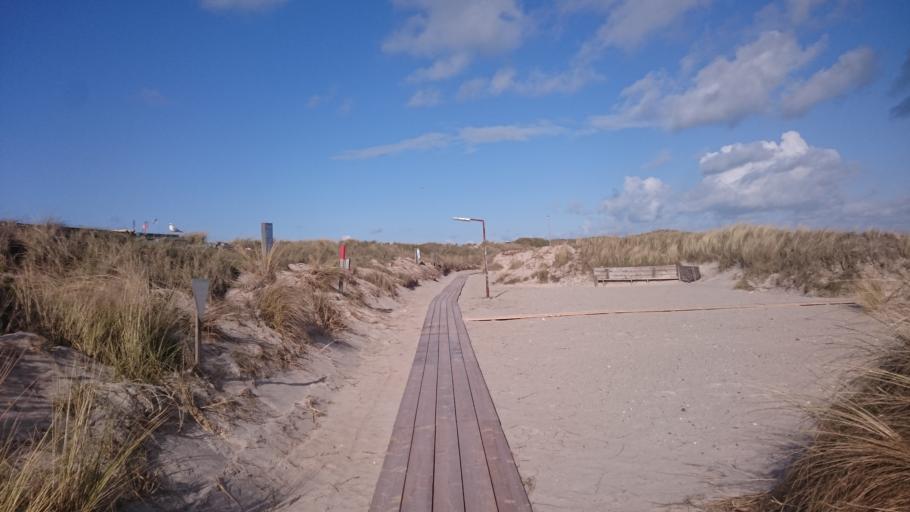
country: DE
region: Schleswig-Holstein
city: Helgoland
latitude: 54.1876
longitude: 7.9117
